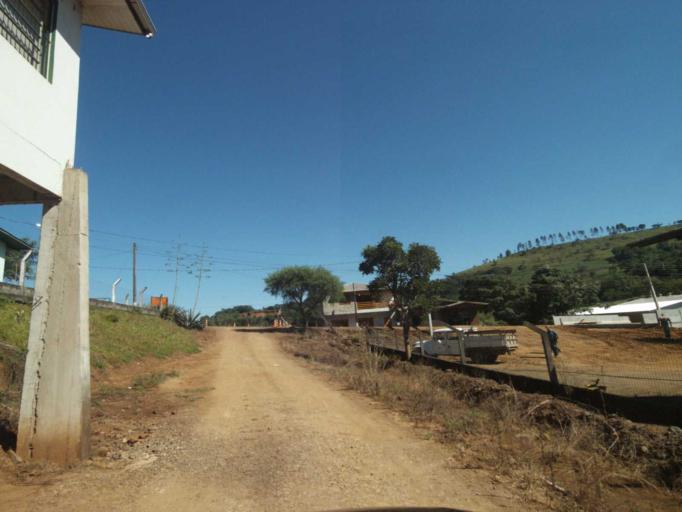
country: BR
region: Parana
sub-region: Francisco Beltrao
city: Francisco Beltrao
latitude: -26.1453
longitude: -53.3138
